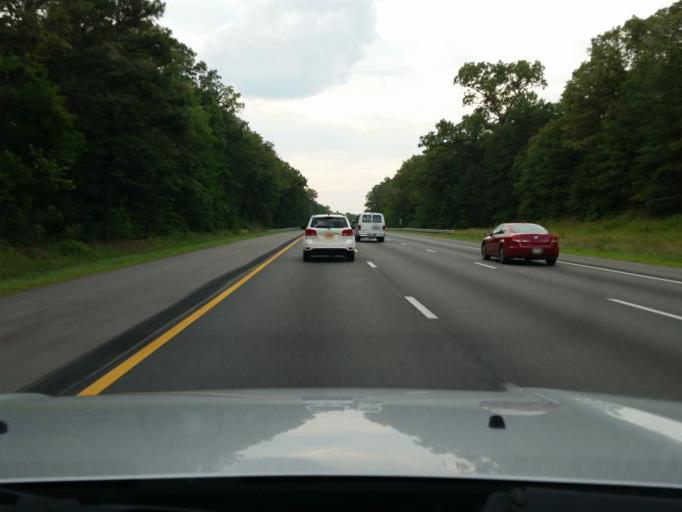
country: US
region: Virginia
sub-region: Caroline County
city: Bowling Green
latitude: 38.0094
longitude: -77.4976
